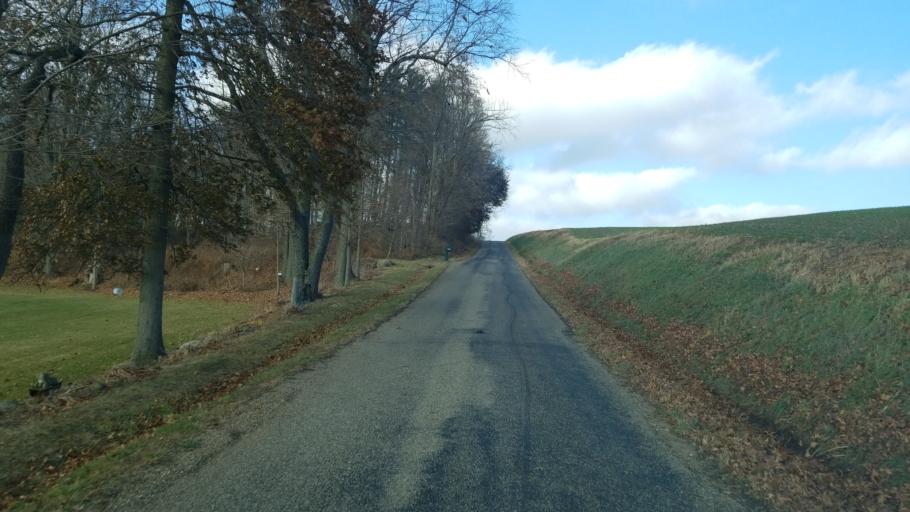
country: US
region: Ohio
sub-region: Ashland County
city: Loudonville
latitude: 40.6563
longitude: -82.3388
